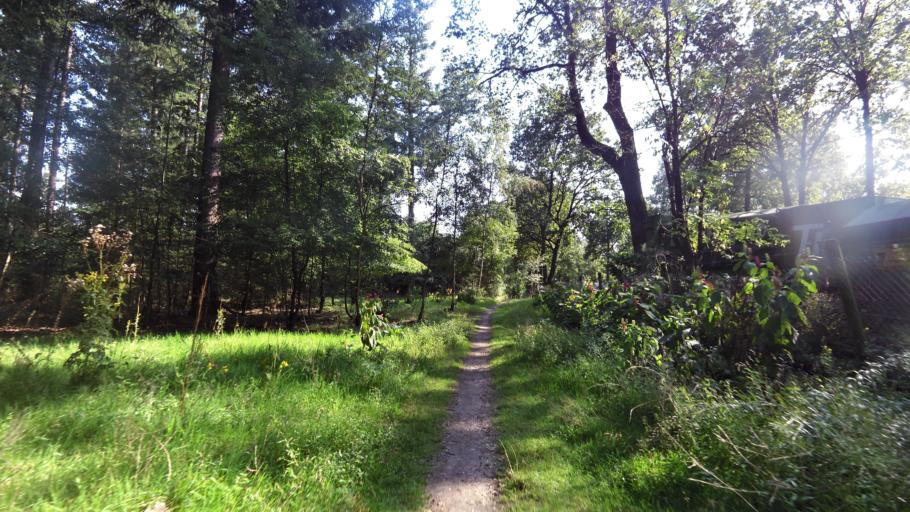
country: NL
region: Gelderland
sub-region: Gemeente Apeldoorn
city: Beekbergen
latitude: 52.1232
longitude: 5.9308
